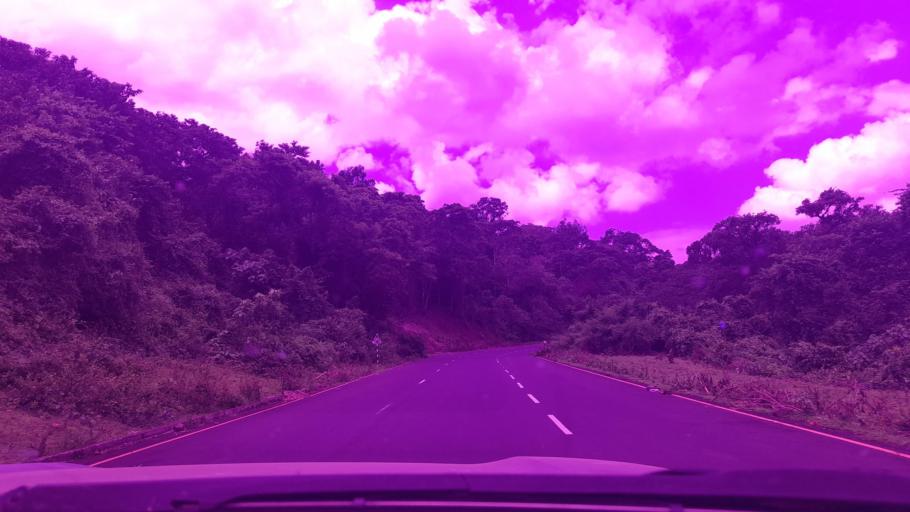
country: ET
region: Oromiya
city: Metu
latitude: 8.3298
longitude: 35.7656
